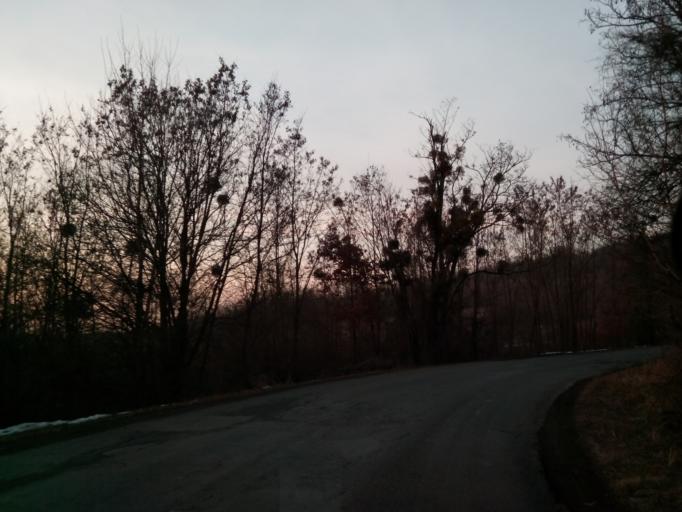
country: HU
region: Borsod-Abauj-Zemplen
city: Gonc
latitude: 48.4875
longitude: 21.3835
